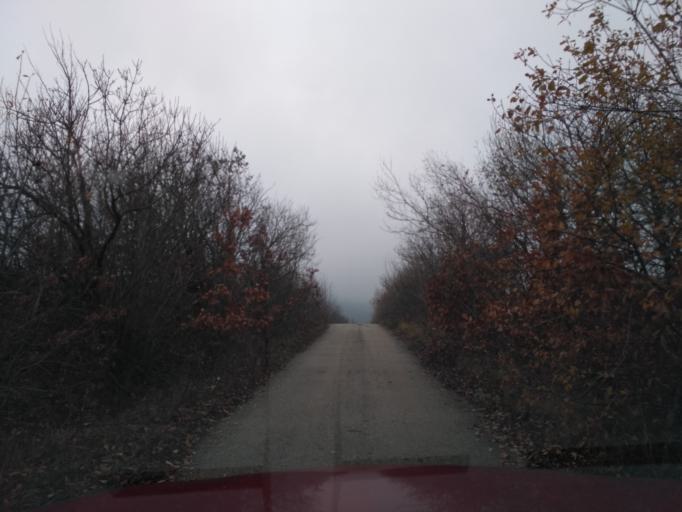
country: SK
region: Kosicky
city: Kosice
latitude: 48.7809
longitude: 21.2154
